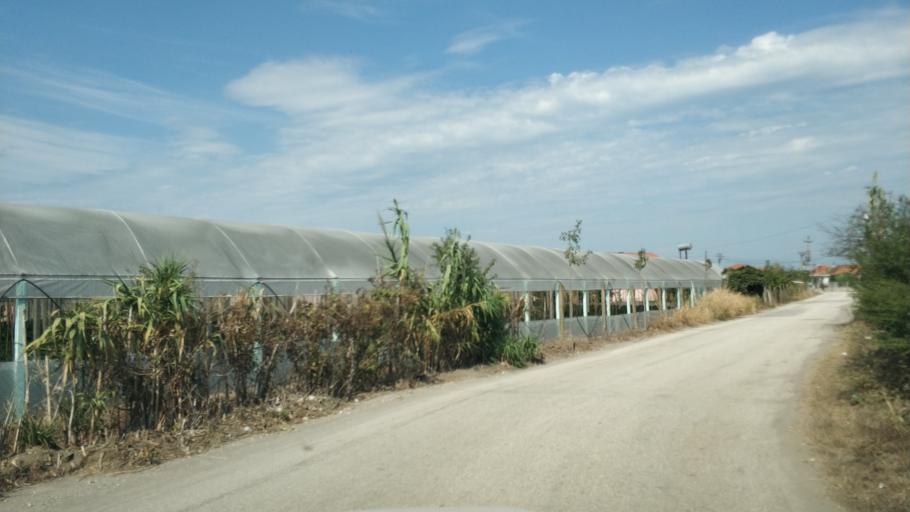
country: AL
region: Fier
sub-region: Rrethi i Lushnjes
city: Divjake
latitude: 40.9895
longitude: 19.5268
